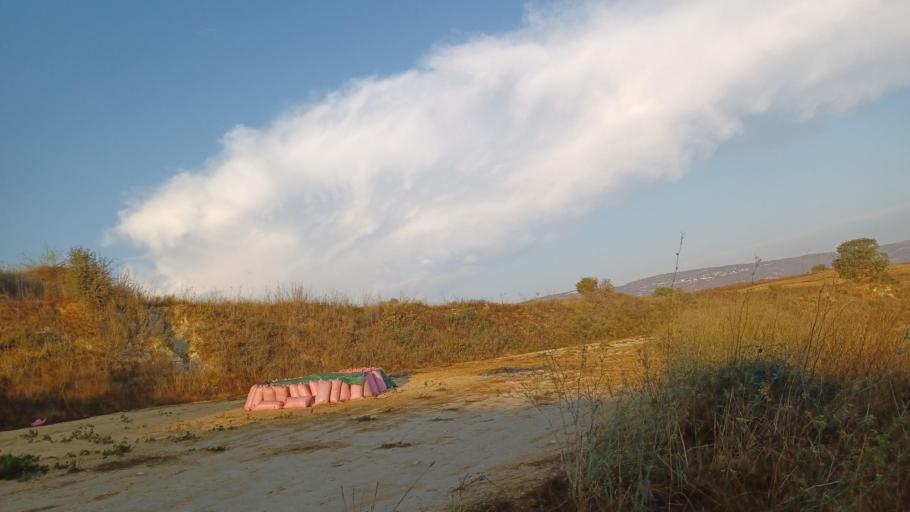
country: CY
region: Pafos
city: Tala
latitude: 34.9017
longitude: 32.4995
